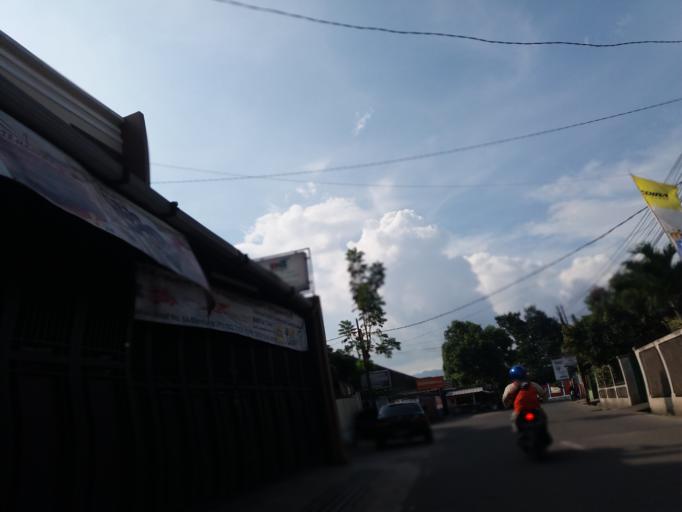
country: ID
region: West Java
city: Bandung
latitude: -6.9319
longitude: 107.6683
